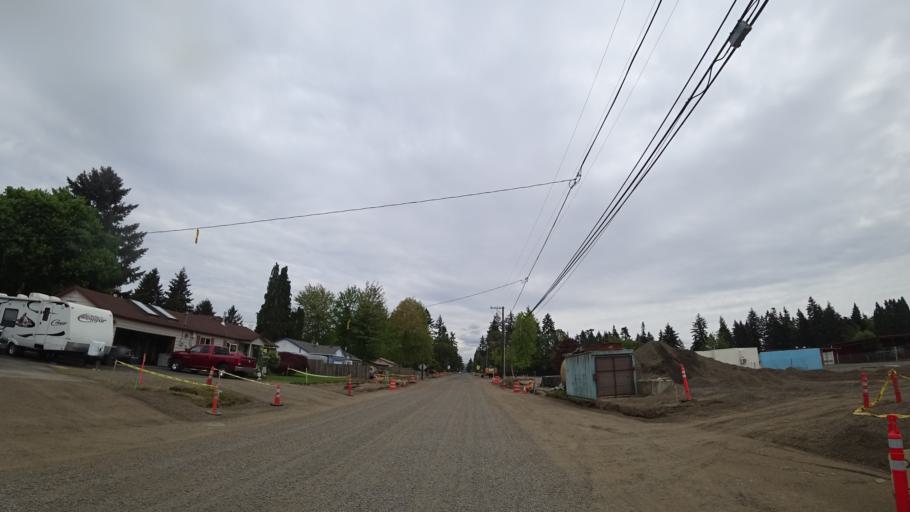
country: US
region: Oregon
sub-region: Washington County
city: Hillsboro
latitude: 45.5161
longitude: -122.9434
